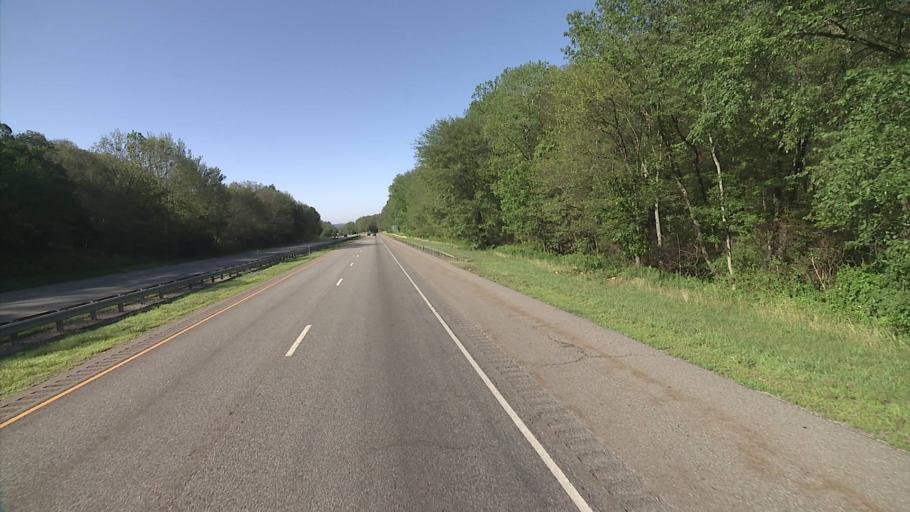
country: US
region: Connecticut
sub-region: Windham County
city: Plainfield
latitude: 41.6910
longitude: -71.9061
